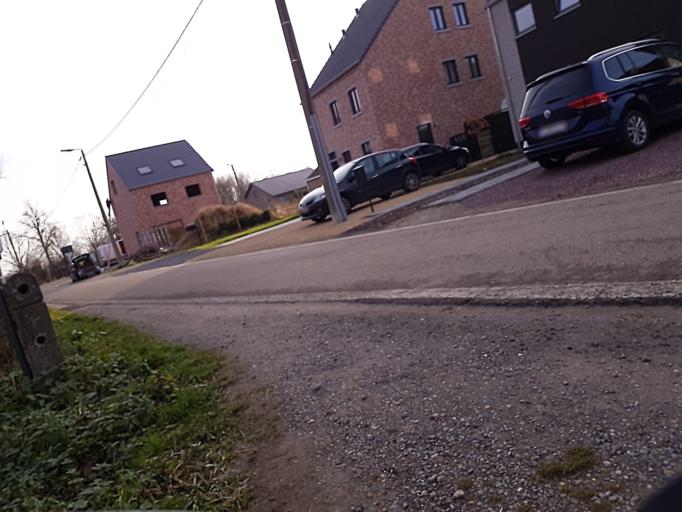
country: BE
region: Flanders
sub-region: Provincie Vlaams-Brabant
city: Rotselaar
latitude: 50.9482
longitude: 4.7017
